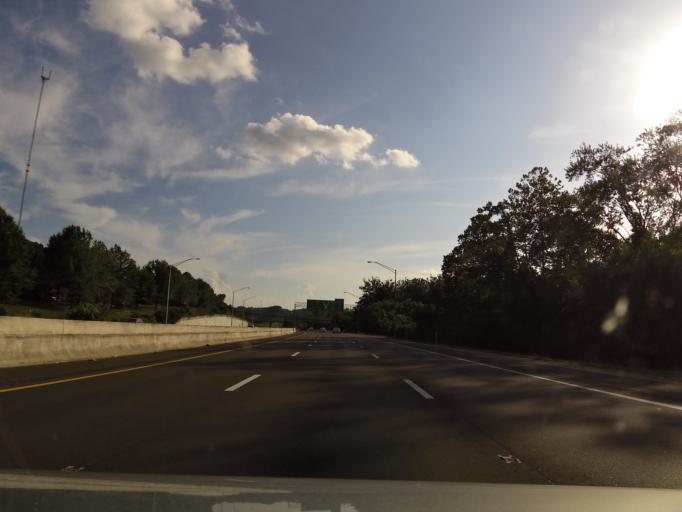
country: US
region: Tennessee
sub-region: Knox County
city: Knoxville
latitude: 36.0057
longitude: -83.9511
